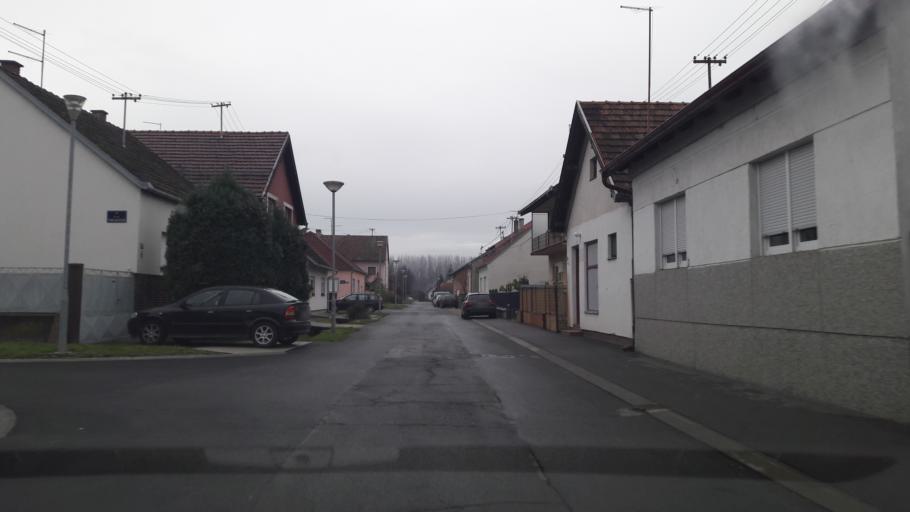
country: HR
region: Osjecko-Baranjska
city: Visnjevac
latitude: 45.5704
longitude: 18.6177
